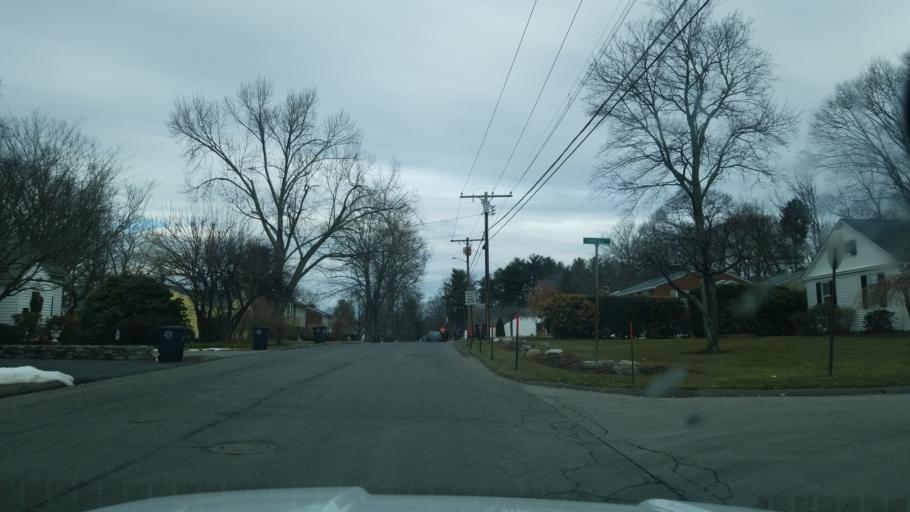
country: US
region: Connecticut
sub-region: Litchfield County
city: Torrington
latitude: 41.8021
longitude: -73.1049
